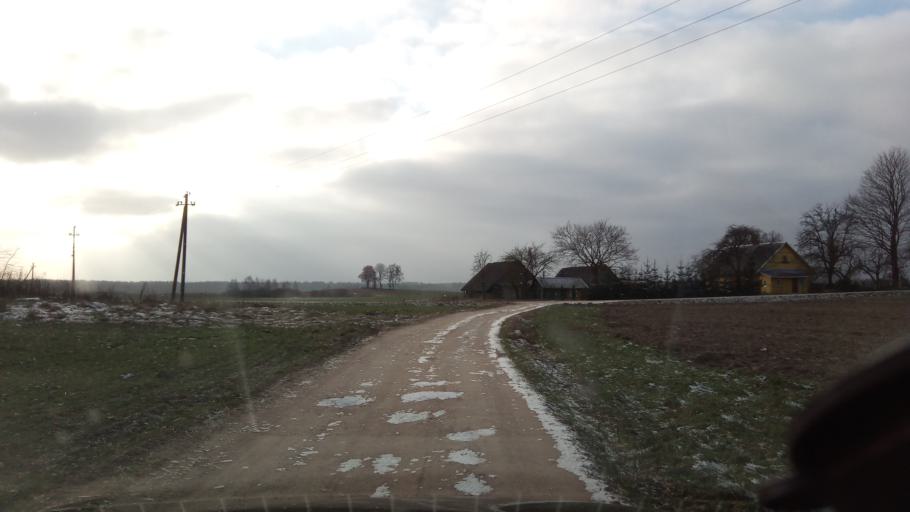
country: LT
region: Alytaus apskritis
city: Varena
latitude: 54.1244
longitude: 24.6599
